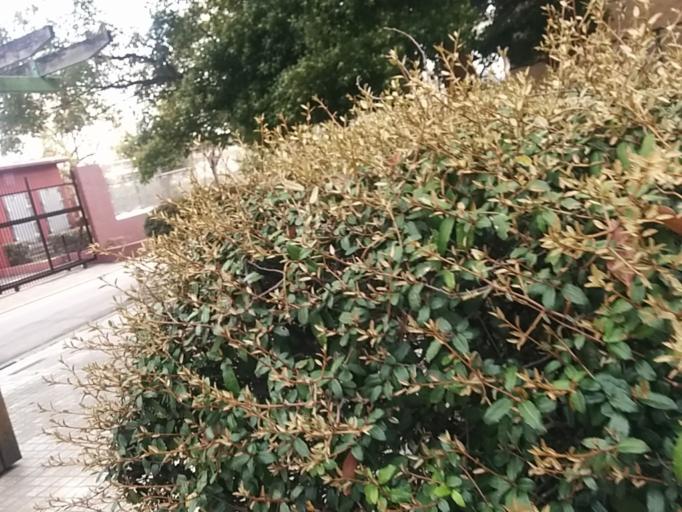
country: JP
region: Tokyo
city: Urayasu
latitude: 35.6751
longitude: 139.8605
